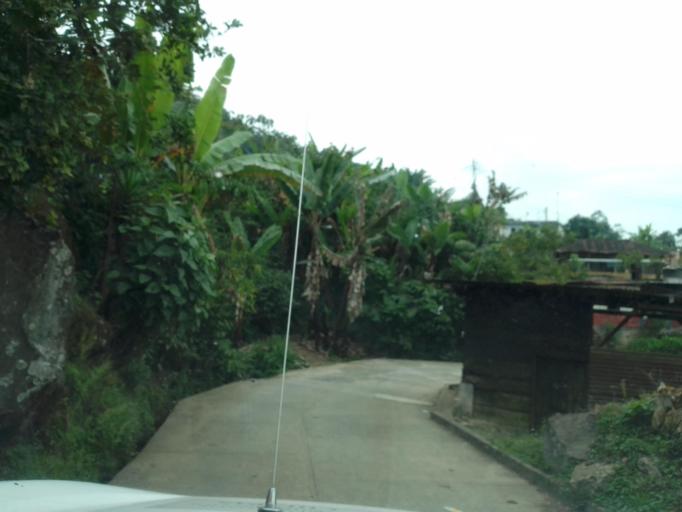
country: MX
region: Chiapas
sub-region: Union Juarez
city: Santo Domingo
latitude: 15.0536
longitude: -92.1142
